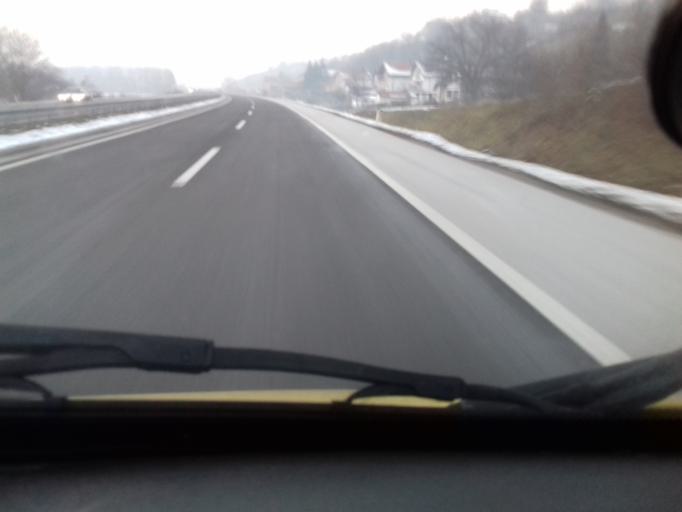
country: BA
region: Federation of Bosnia and Herzegovina
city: Visoko
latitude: 43.9943
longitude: 18.1924
